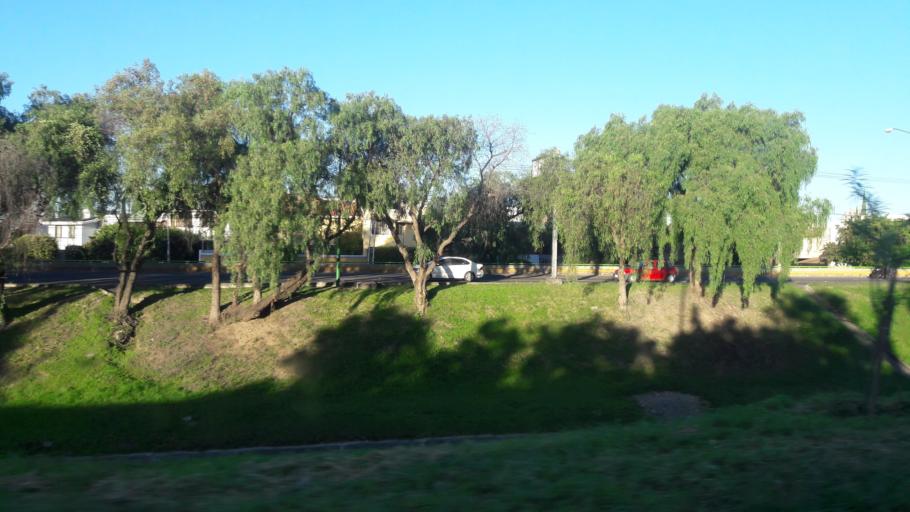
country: MX
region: Guanajuato
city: Leon
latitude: 21.1096
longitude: -101.6630
